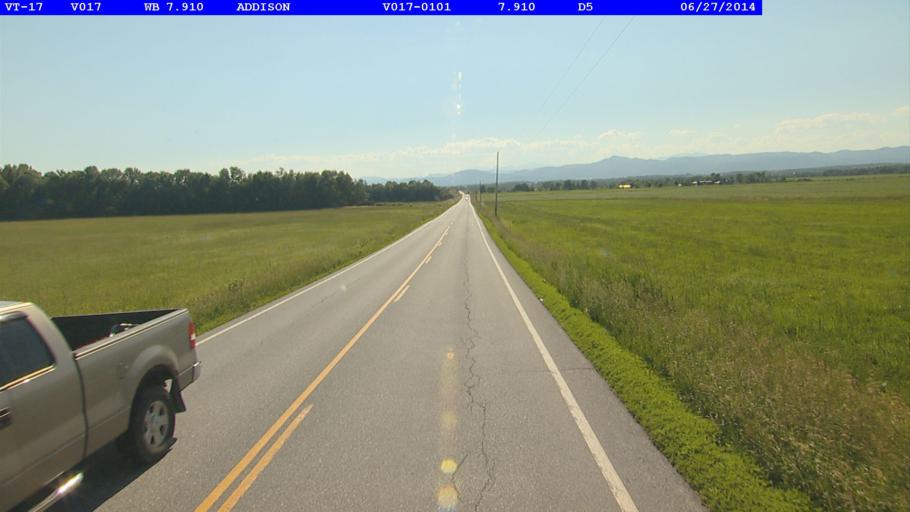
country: US
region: Vermont
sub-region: Addison County
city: Vergennes
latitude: 44.0882
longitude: -73.3118
